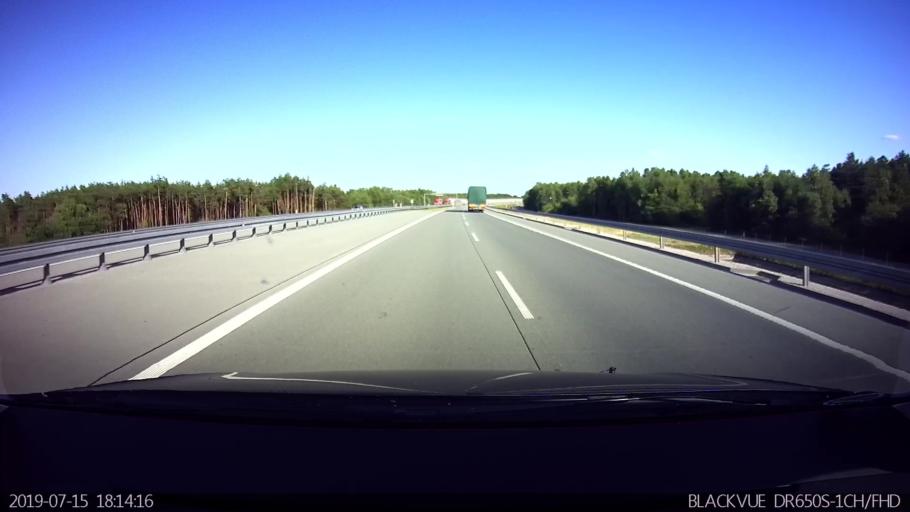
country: PL
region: Lodz Voivodeship
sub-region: Powiat zdunskowolski
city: Zapolice
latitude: 51.5941
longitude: 18.8845
